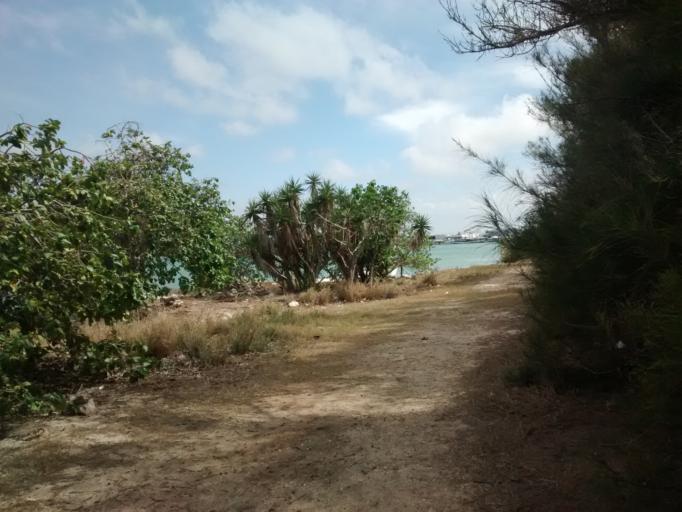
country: MX
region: Yucatan
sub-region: Progreso
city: Chelem
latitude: 21.2785
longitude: -89.7031
